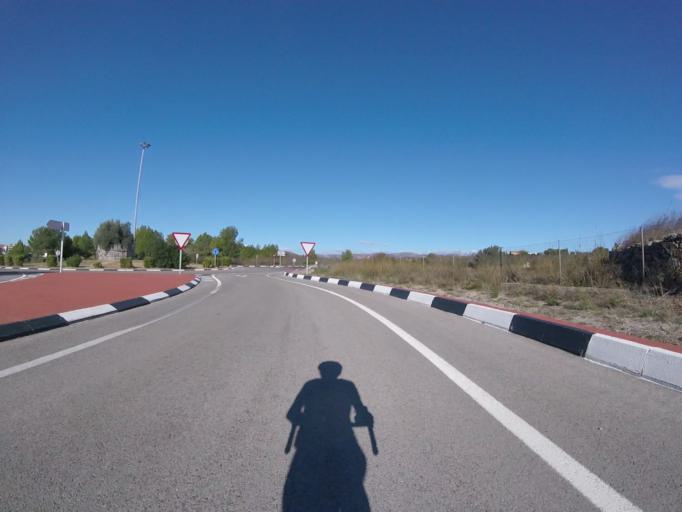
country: ES
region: Valencia
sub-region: Provincia de Castello
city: Chert/Xert
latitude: 40.4659
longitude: 0.1871
